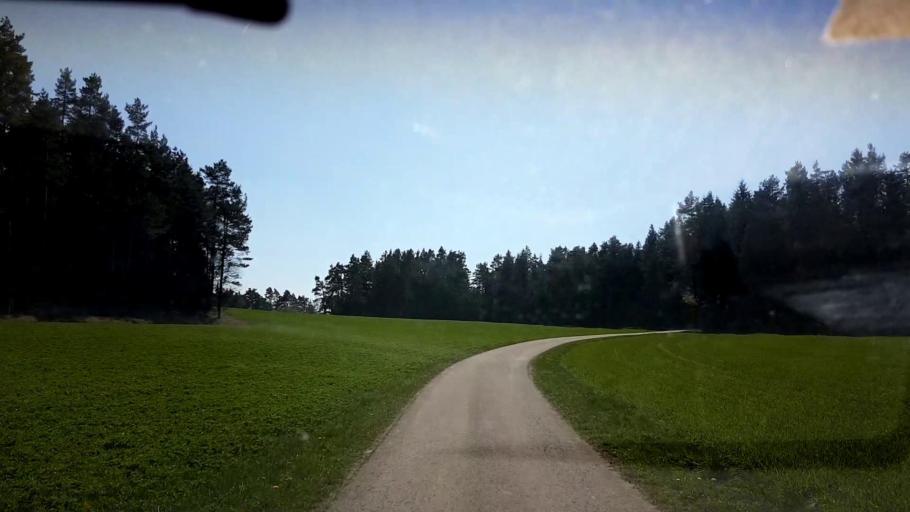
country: DE
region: Bavaria
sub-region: Upper Franconia
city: Konigsfeld
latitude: 49.9082
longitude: 11.1765
